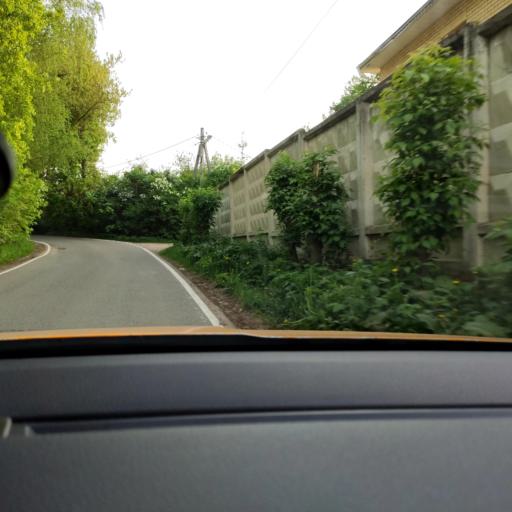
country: RU
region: Moskovskaya
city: Selyatino
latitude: 55.5291
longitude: 37.0001
